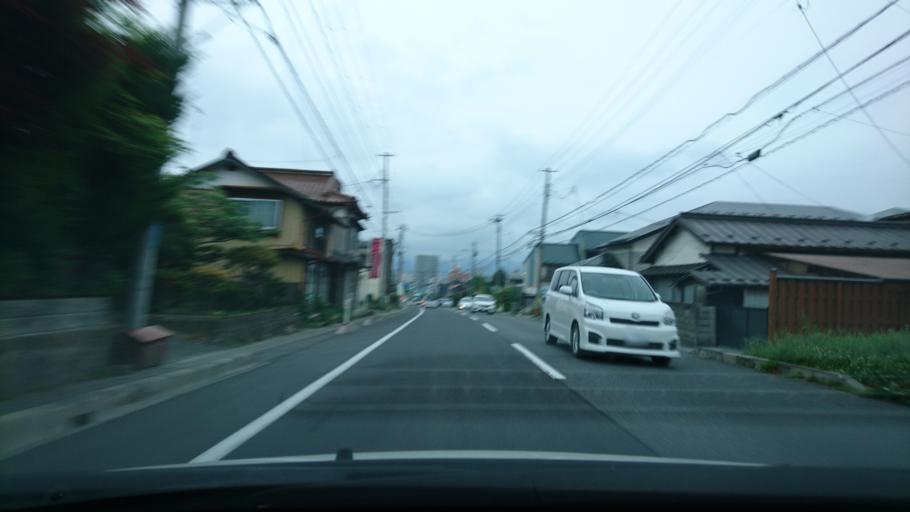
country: JP
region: Iwate
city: Ichinoseki
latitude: 38.9208
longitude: 141.1324
